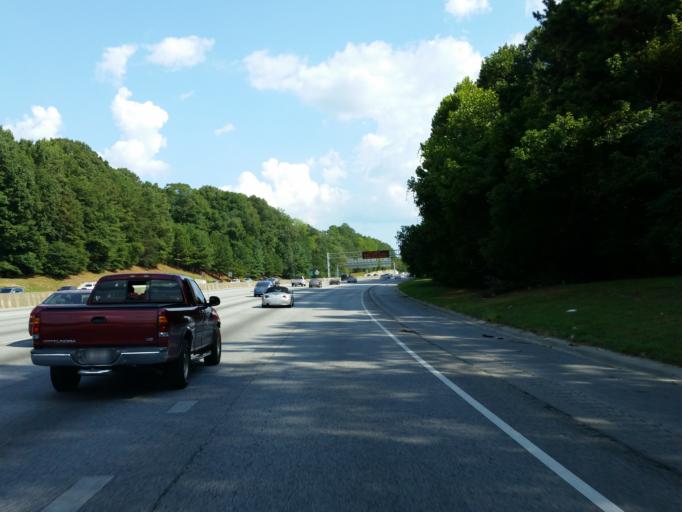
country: US
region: Georgia
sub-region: Cobb County
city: Vinings
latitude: 33.8730
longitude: -84.4455
